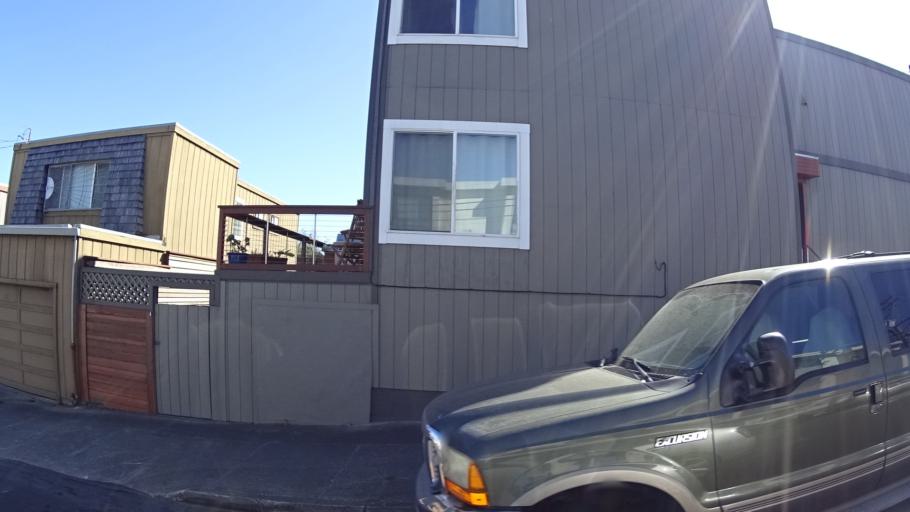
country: US
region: California
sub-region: San Mateo County
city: Daly City
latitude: 37.7265
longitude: -122.4182
